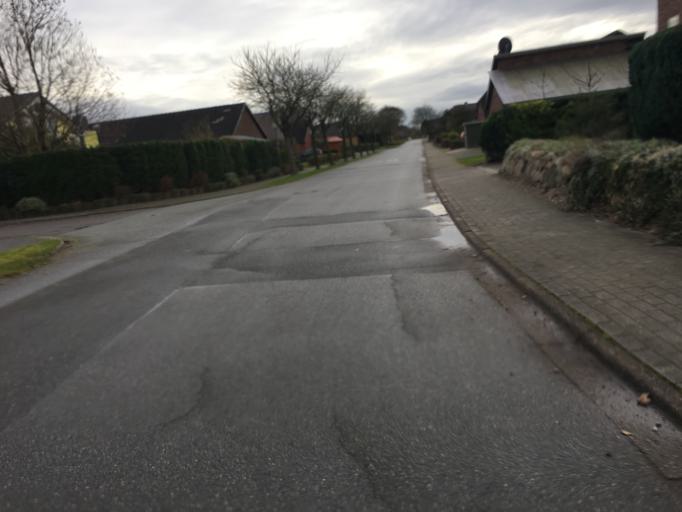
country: DE
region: Schleswig-Holstein
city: Wanderup
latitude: 54.6941
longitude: 9.3381
